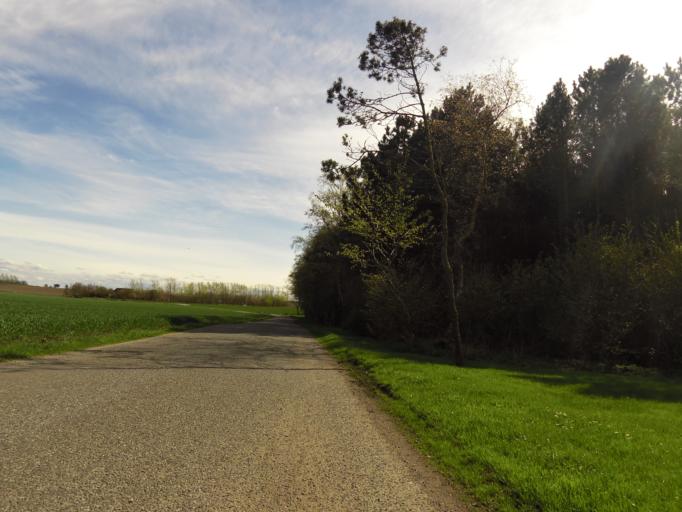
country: DK
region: Central Jutland
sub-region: Skive Kommune
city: Skive
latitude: 56.5494
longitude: 8.9623
